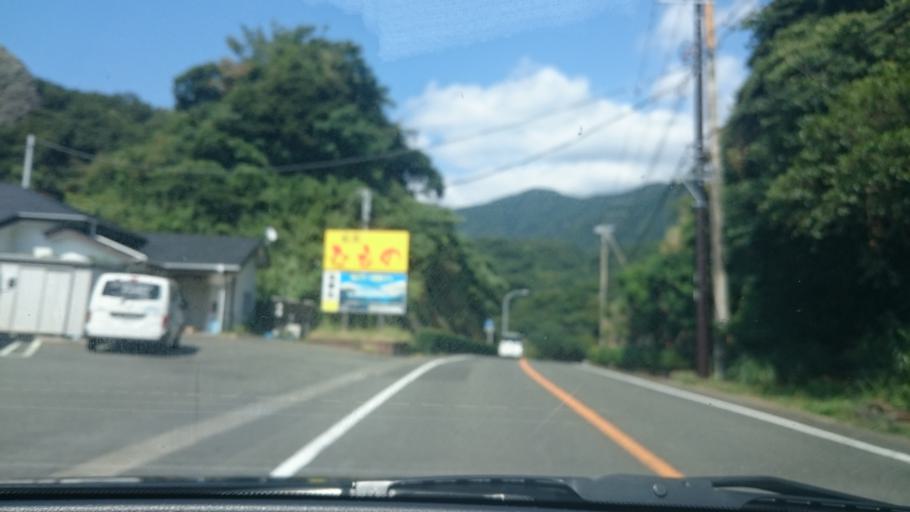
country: JP
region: Shizuoka
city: Heda
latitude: 34.7983
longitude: 138.7676
